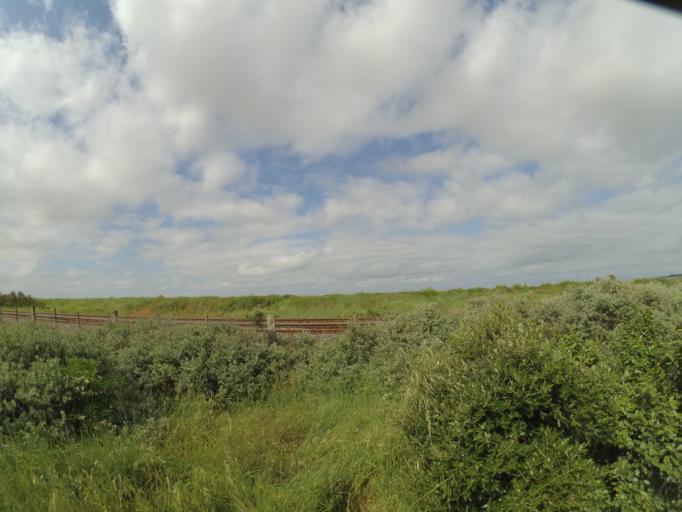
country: FR
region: Poitou-Charentes
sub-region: Departement de la Charente-Maritime
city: Angoulins
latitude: 46.0896
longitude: -1.0985
